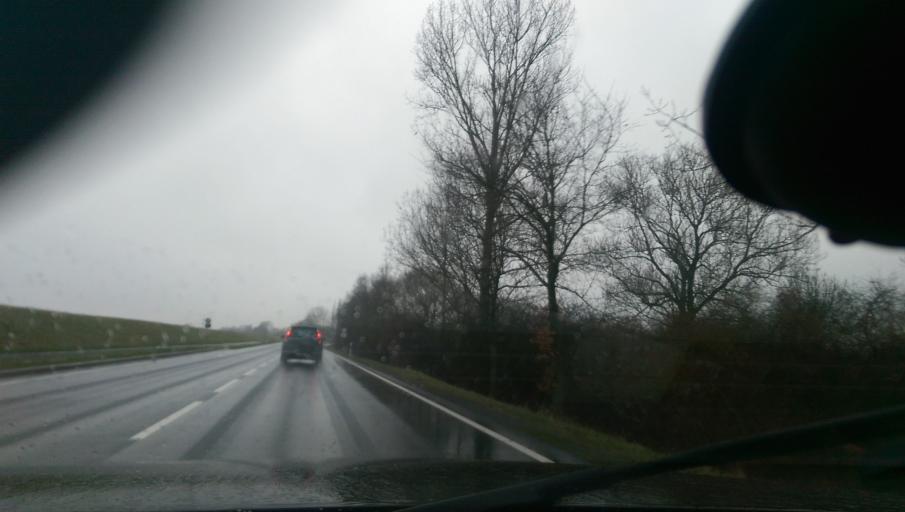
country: DE
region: Lower Saxony
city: Dorverden
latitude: 52.8764
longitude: 9.2235
